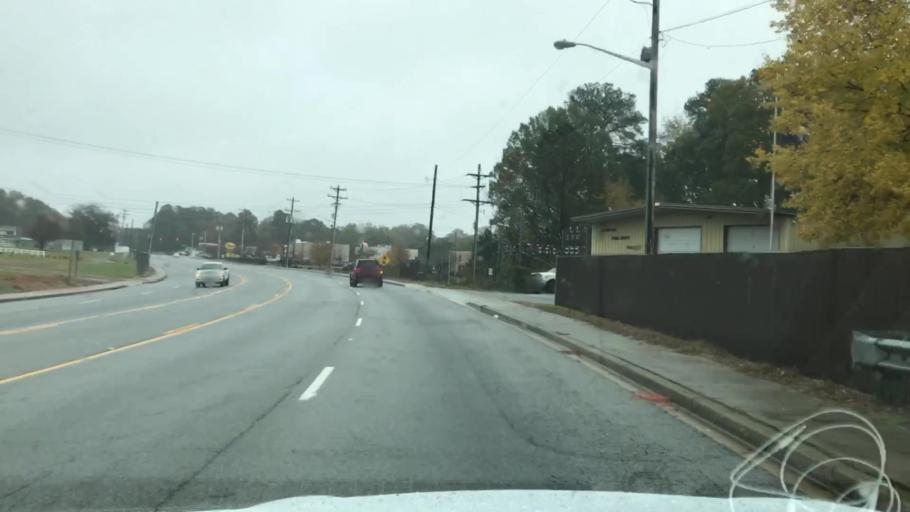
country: US
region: South Carolina
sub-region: Laurens County
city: Clinton
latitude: 34.4531
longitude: -81.8796
